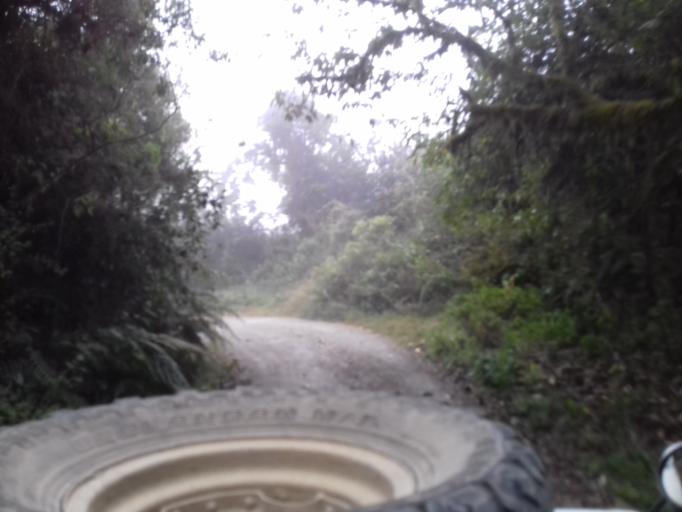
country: CO
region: Quindio
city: Salento
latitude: 4.5538
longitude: -75.5111
